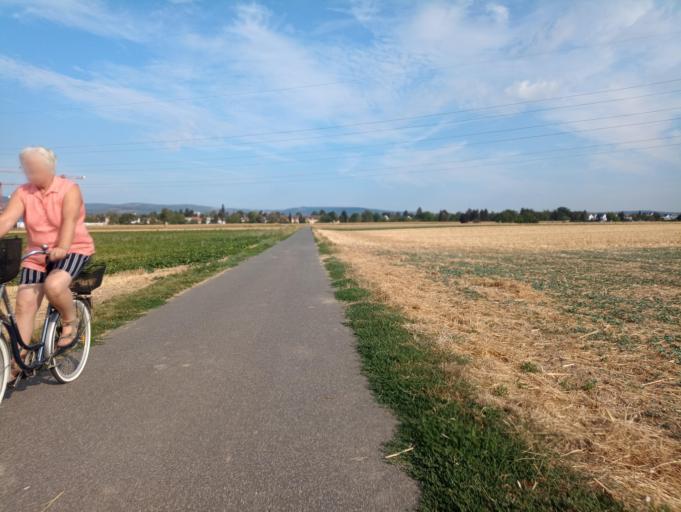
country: DE
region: Hesse
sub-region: Regierungsbezirk Darmstadt
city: Oberursel
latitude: 50.1907
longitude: 8.6002
